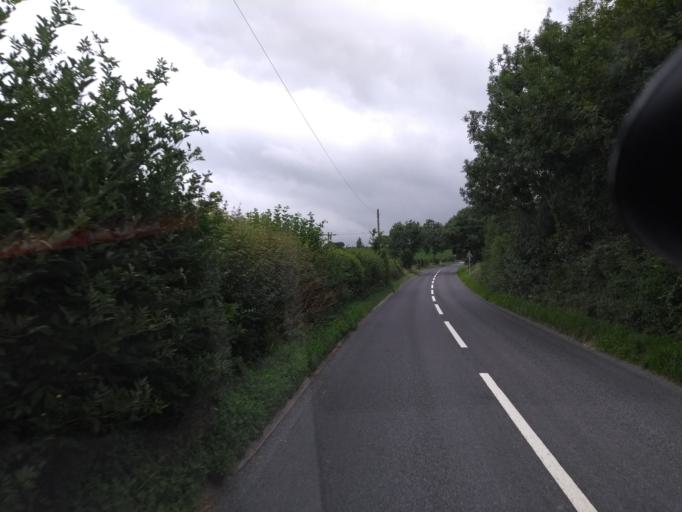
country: GB
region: England
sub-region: Somerset
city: Merriott
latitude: 50.9276
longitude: -2.7678
